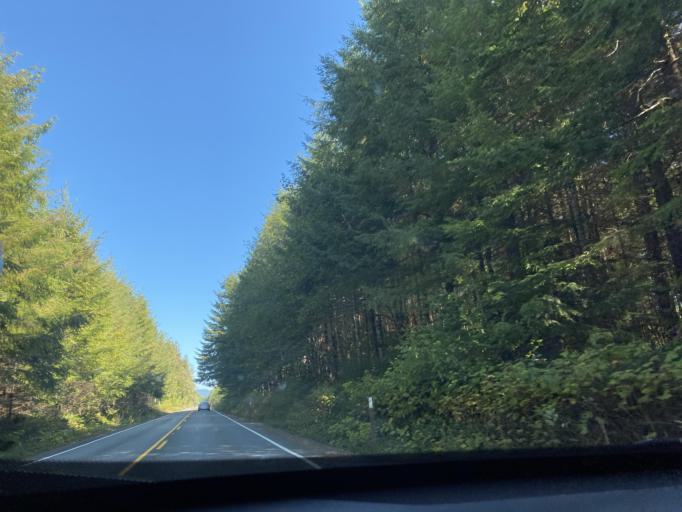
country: US
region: Washington
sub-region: Clallam County
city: Forks
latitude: 47.9233
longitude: -124.4995
